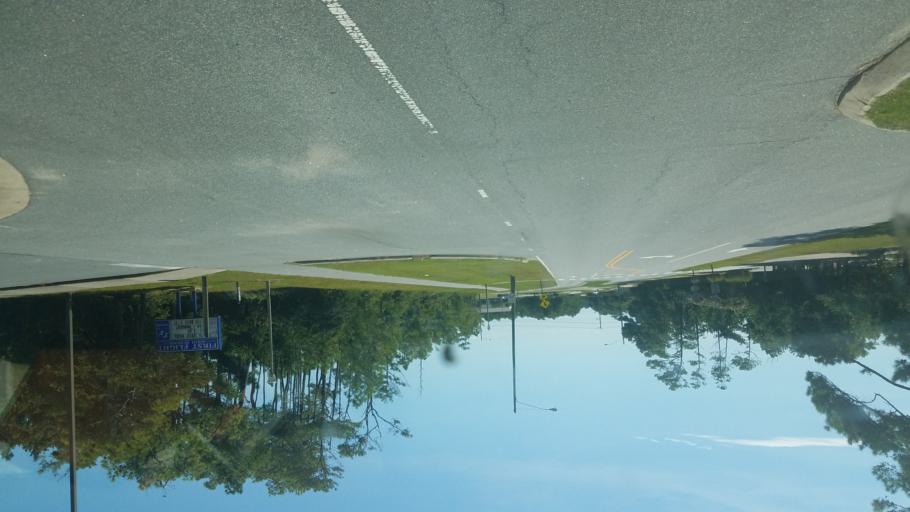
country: US
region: North Carolina
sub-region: Dare County
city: Kill Devil Hills
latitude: 36.0098
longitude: -75.6650
